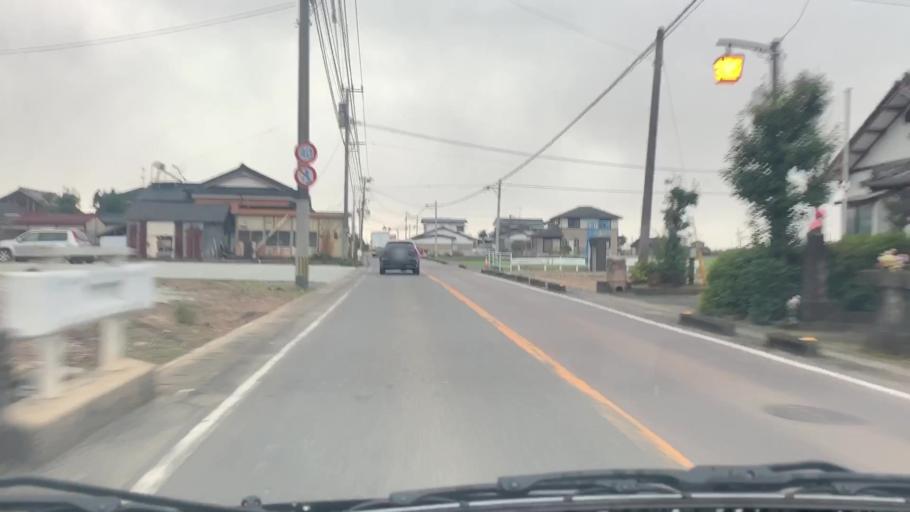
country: JP
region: Saga Prefecture
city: Takeocho-takeo
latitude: 33.2056
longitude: 130.0892
